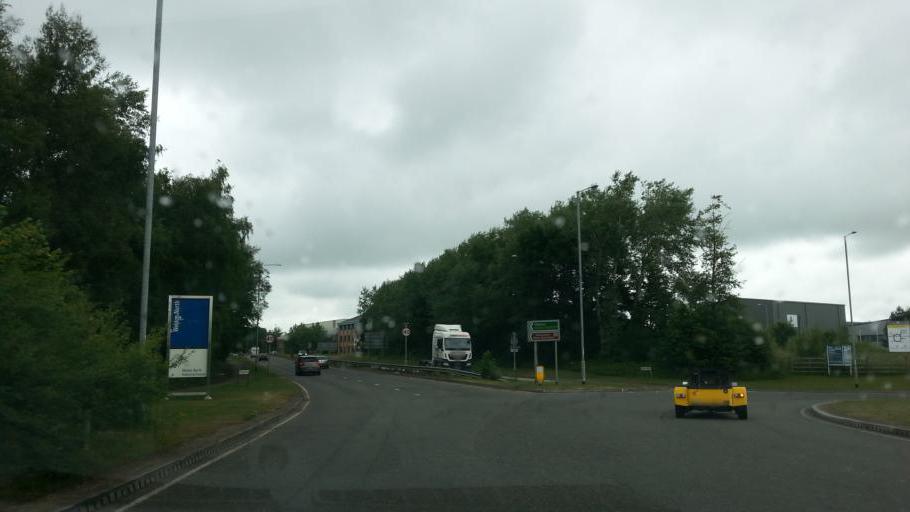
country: GB
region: England
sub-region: Northamptonshire
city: Corby
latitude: 52.4996
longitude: -0.6470
